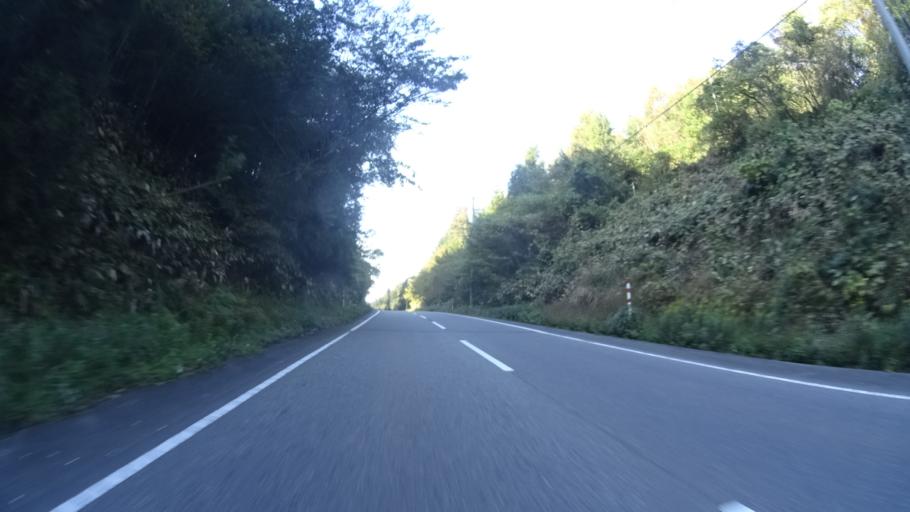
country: JP
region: Ishikawa
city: Hakui
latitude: 37.0102
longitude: 136.7991
